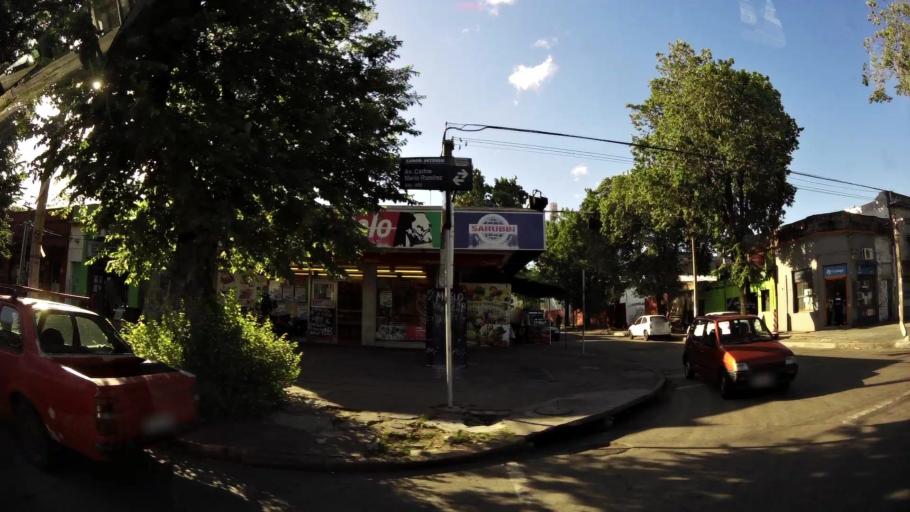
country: UY
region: Montevideo
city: Montevideo
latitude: -34.8624
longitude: -56.2316
